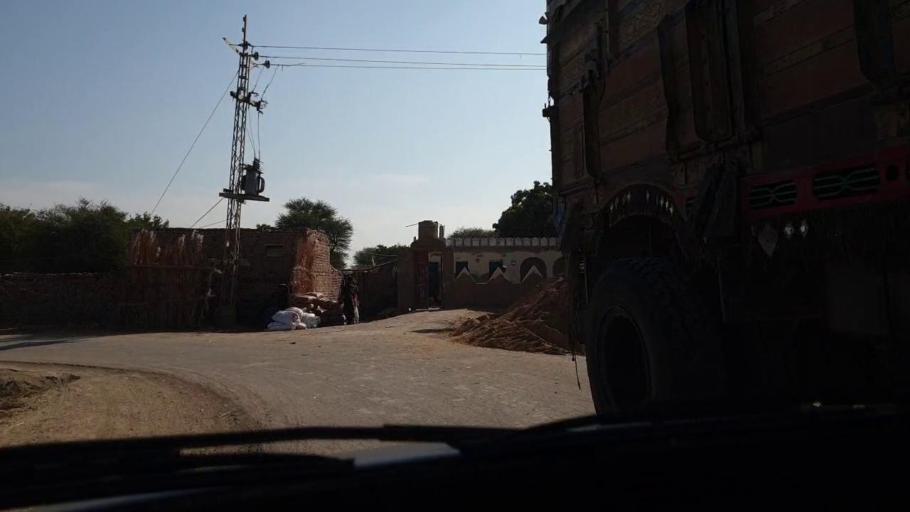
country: PK
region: Sindh
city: Bulri
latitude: 24.9568
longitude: 68.4195
